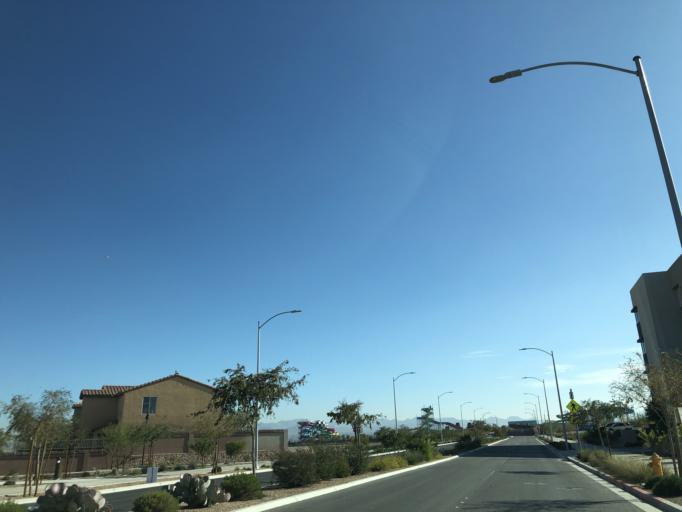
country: US
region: Nevada
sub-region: Clark County
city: Whitney
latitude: 36.0748
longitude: -115.0295
